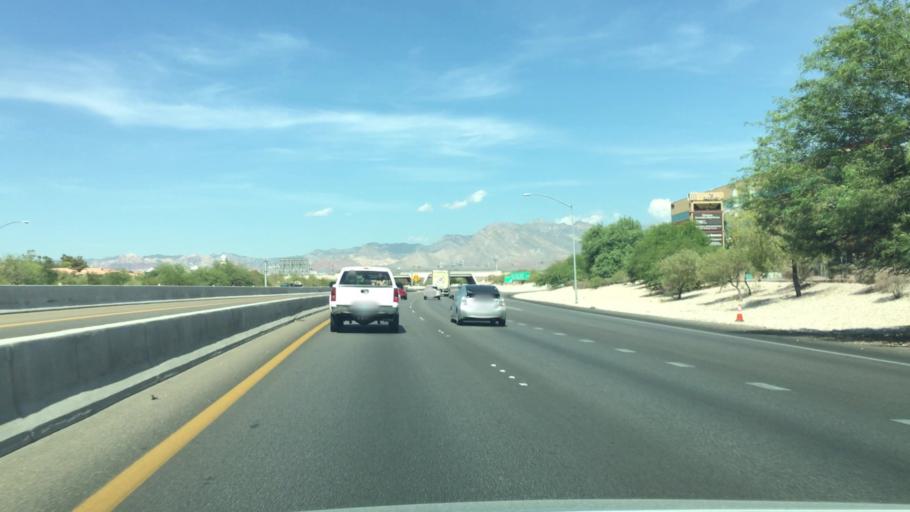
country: US
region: Nevada
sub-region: Clark County
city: Spring Valley
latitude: 36.1784
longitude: -115.2542
